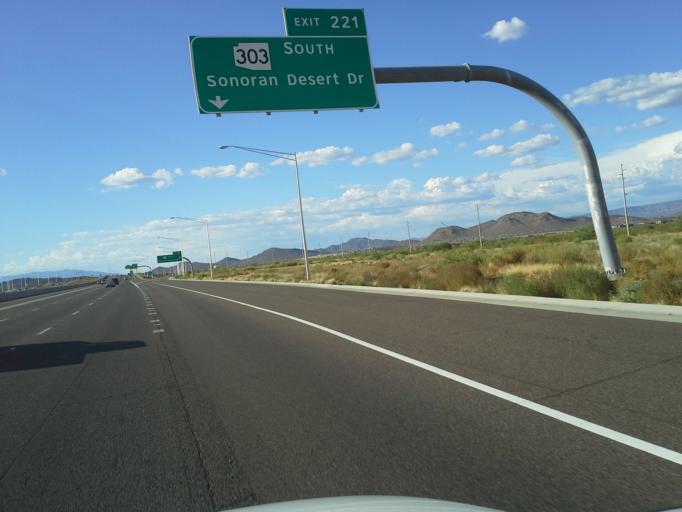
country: US
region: Arizona
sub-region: Maricopa County
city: Anthem
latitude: 33.7613
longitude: -112.1274
